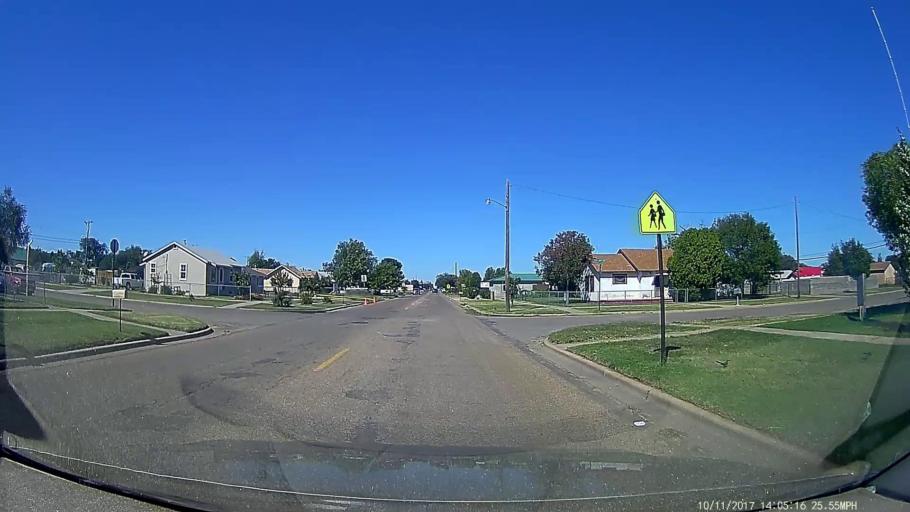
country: US
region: New Mexico
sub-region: Curry County
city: Clovis
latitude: 34.4014
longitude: -103.2142
